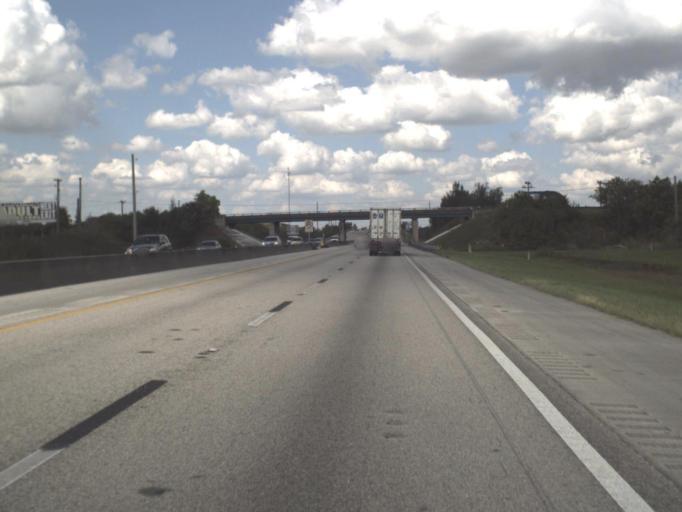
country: US
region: Florida
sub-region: Saint Lucie County
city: Fort Pierce South
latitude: 27.3730
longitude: -80.3831
